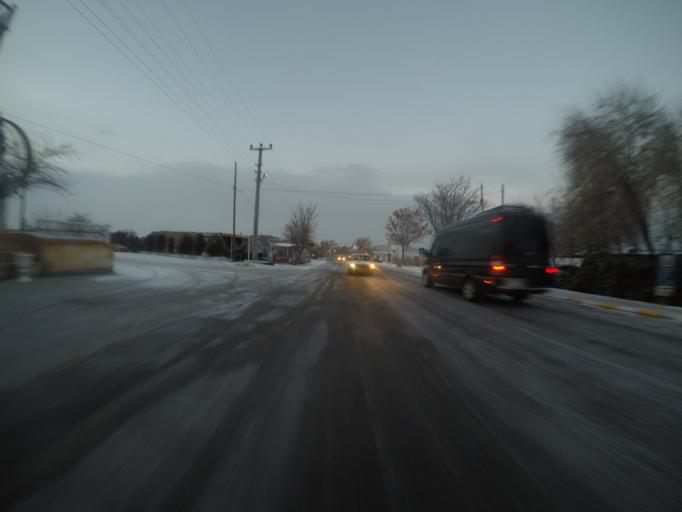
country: TR
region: Nevsehir
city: Goereme
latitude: 38.6205
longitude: 34.8045
